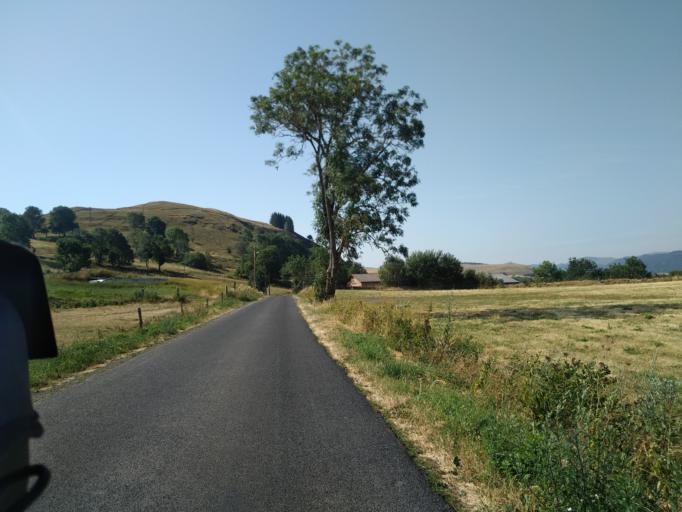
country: FR
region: Auvergne
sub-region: Departement du Cantal
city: Riom-es-Montagnes
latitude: 45.2481
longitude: 2.7427
